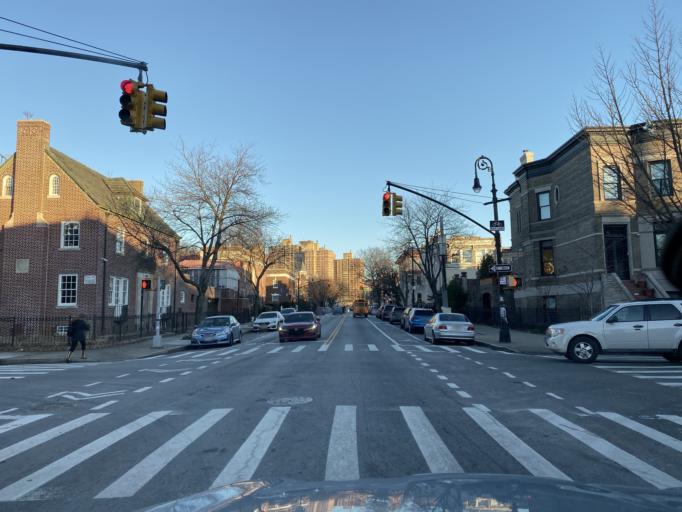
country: US
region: New York
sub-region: Kings County
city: Brooklyn
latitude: 40.6589
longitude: -73.9594
